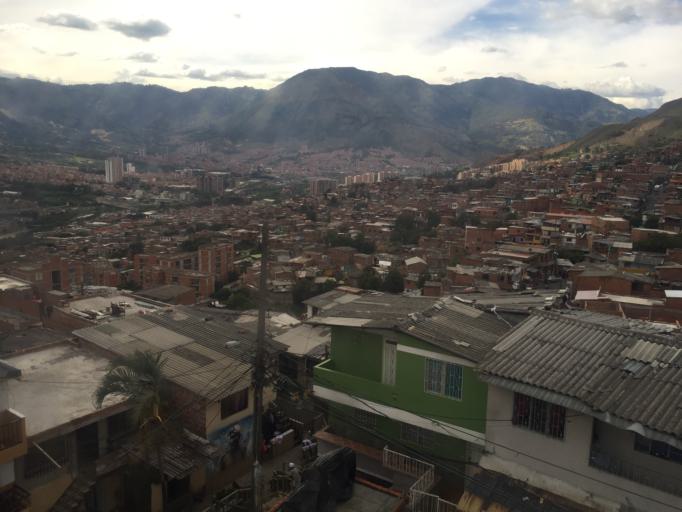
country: CO
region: Antioquia
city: Bello
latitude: 6.2960
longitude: -75.5509
